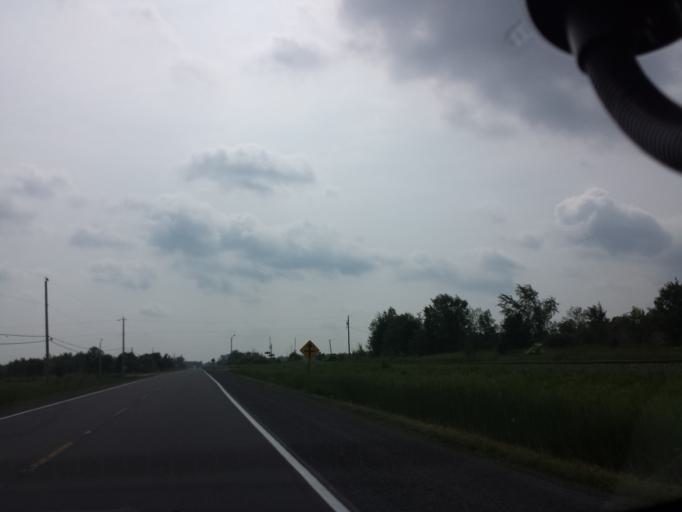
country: CA
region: Ontario
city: Clarence-Rockland
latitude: 45.3659
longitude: -75.4374
